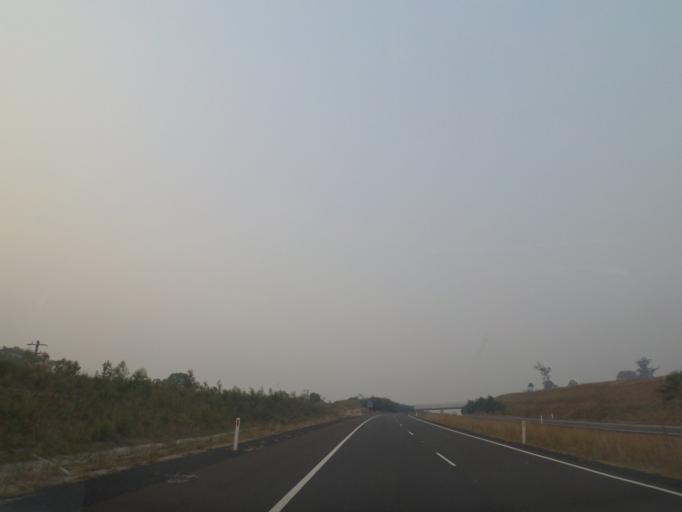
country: AU
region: New South Wales
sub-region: Nambucca Shire
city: Macksville
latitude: -30.7594
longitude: 152.9046
